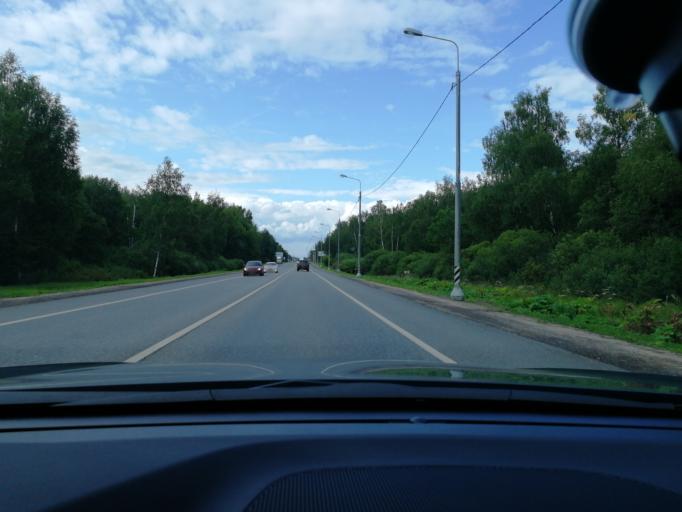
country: RU
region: Moskovskaya
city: Proletarskiy
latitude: 55.0569
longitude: 37.4342
